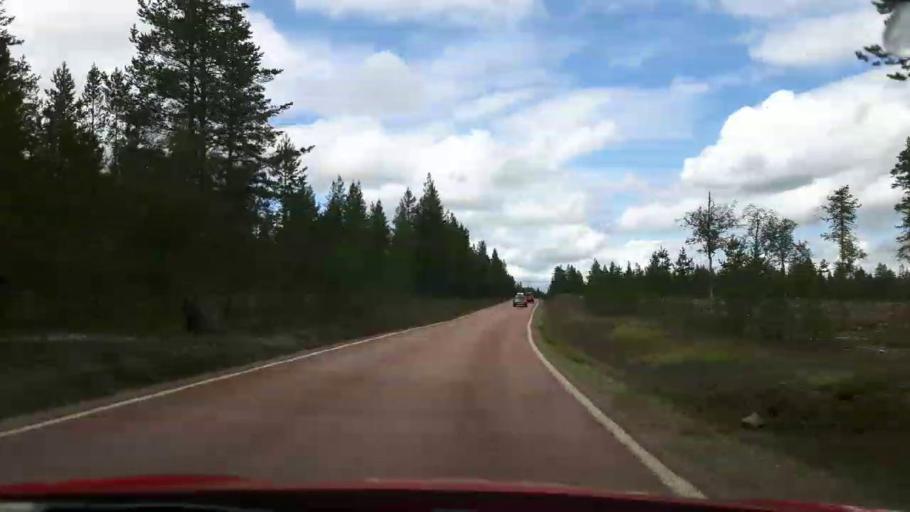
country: NO
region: Hedmark
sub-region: Trysil
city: Innbygda
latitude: 61.8525
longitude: 12.9506
